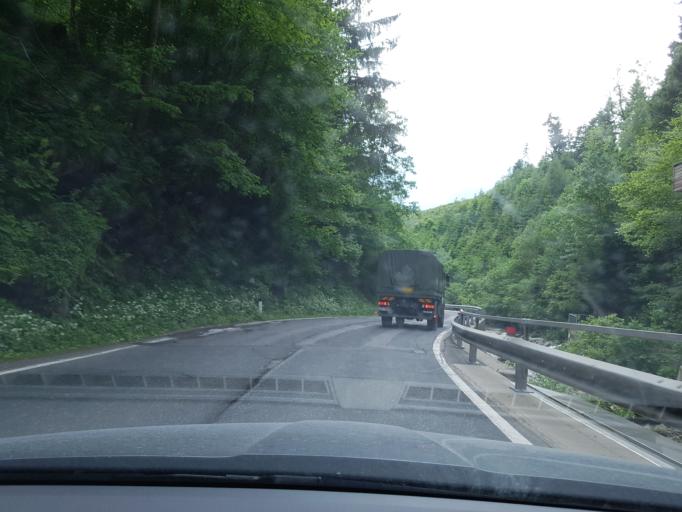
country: AT
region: Carinthia
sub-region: Politischer Bezirk Villach Land
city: Feld am See
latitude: 46.8014
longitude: 13.7532
